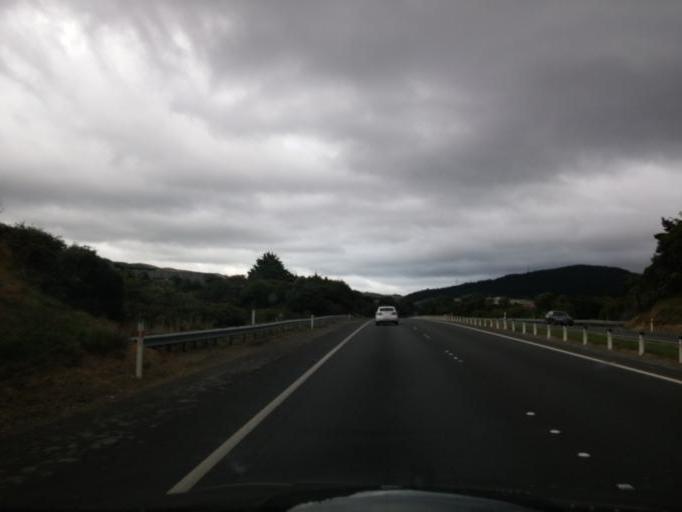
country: NZ
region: Wellington
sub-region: Porirua City
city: Porirua
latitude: -41.1720
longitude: 174.8312
